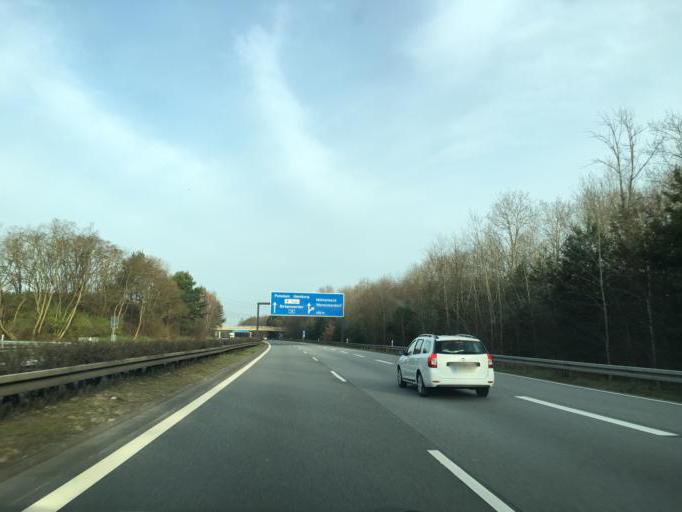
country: DE
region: Berlin
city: Blankenfelde
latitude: 52.6778
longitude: 13.3908
